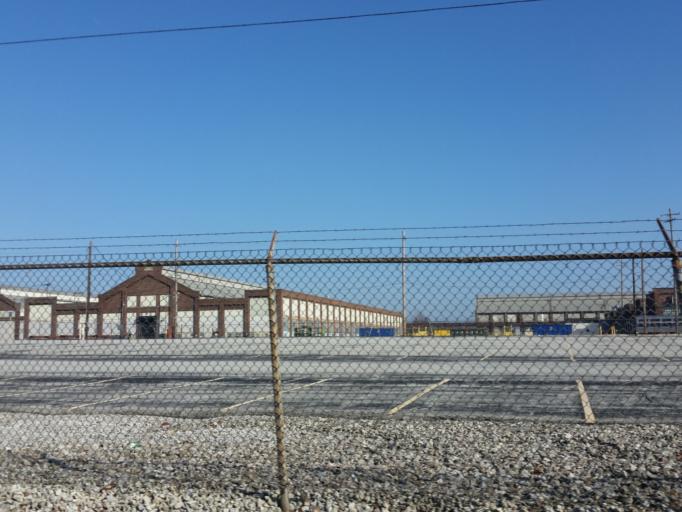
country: US
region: Indiana
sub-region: Marion County
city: Beech Grove
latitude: 39.7166
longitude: -86.0777
